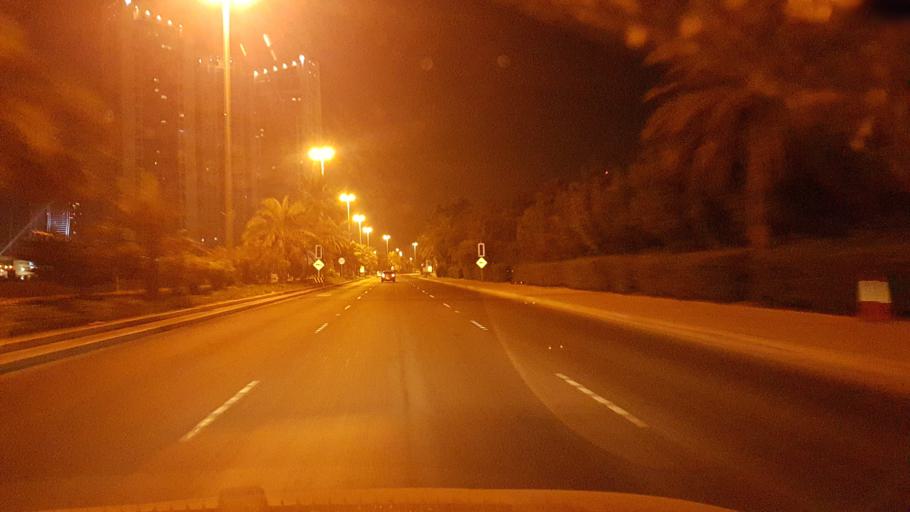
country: BH
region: Manama
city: Jidd Hafs
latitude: 26.2259
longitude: 50.5616
